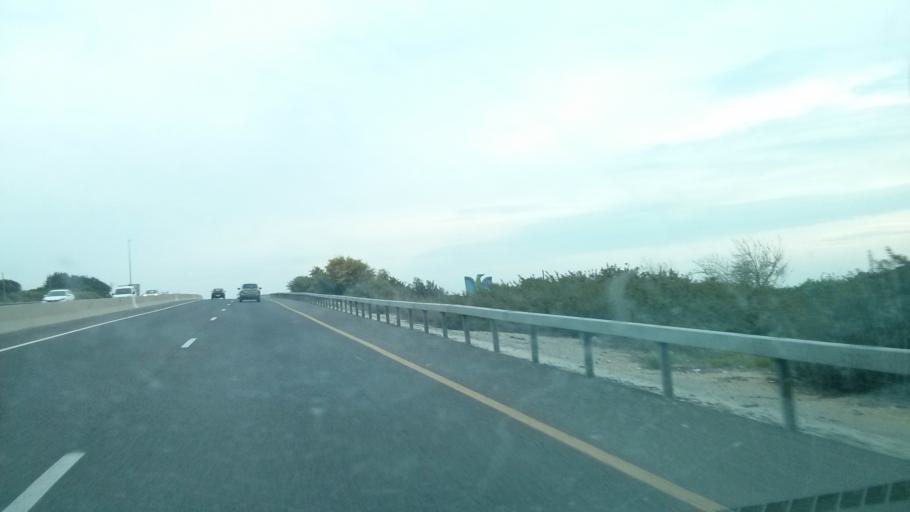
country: IL
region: Haifa
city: Hadera
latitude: 32.4630
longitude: 34.8960
